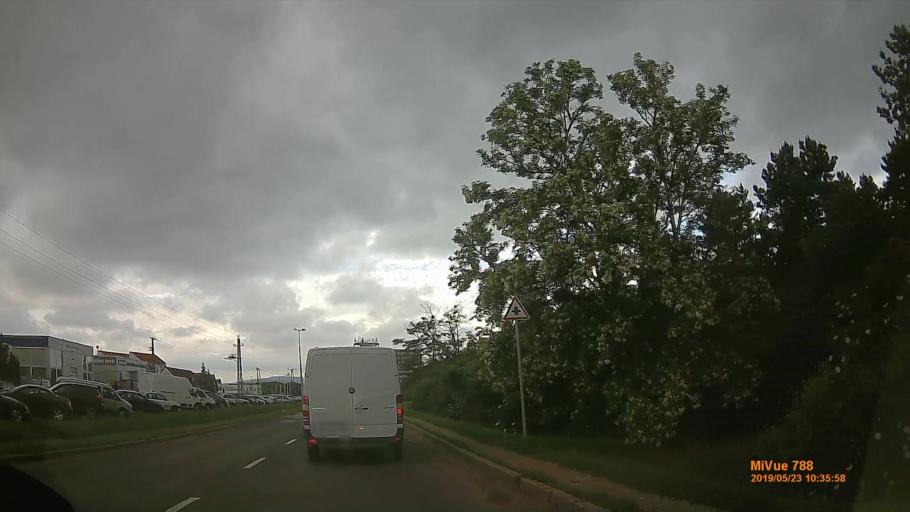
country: HU
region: Veszprem
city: Veszprem
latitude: 47.1117
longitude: 17.8865
